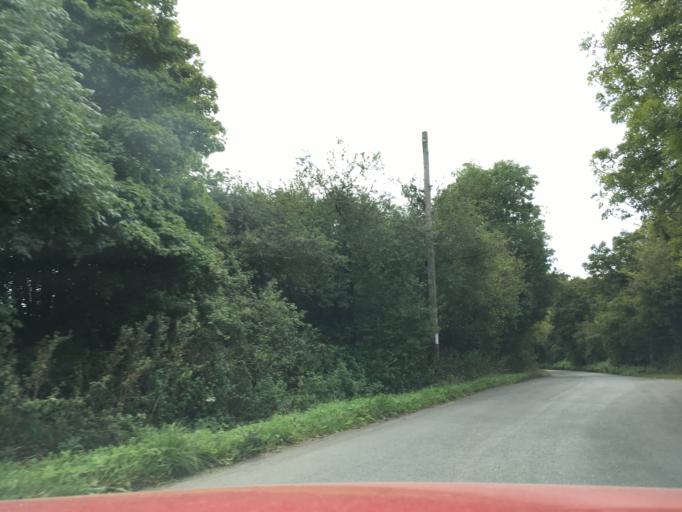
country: GB
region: England
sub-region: Gloucestershire
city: Berkeley
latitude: 51.6726
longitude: -2.4204
